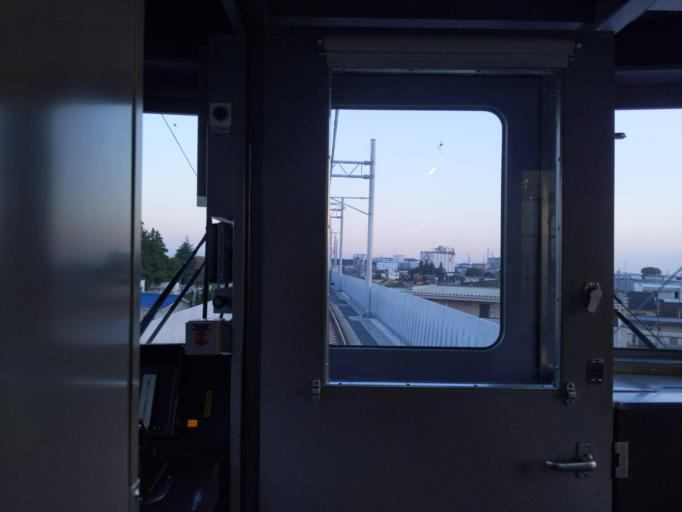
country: JP
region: Chiba
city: Noda
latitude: 35.9457
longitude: 139.8684
